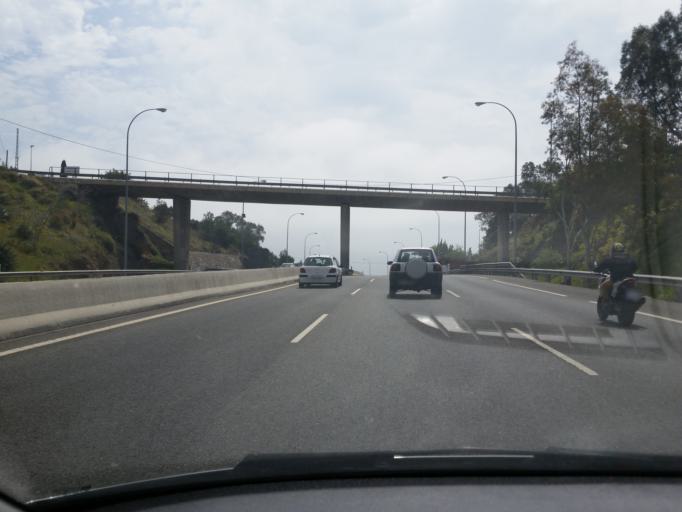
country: ES
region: Andalusia
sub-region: Provincia de Malaga
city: Malaga
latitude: 36.7471
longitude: -4.4090
